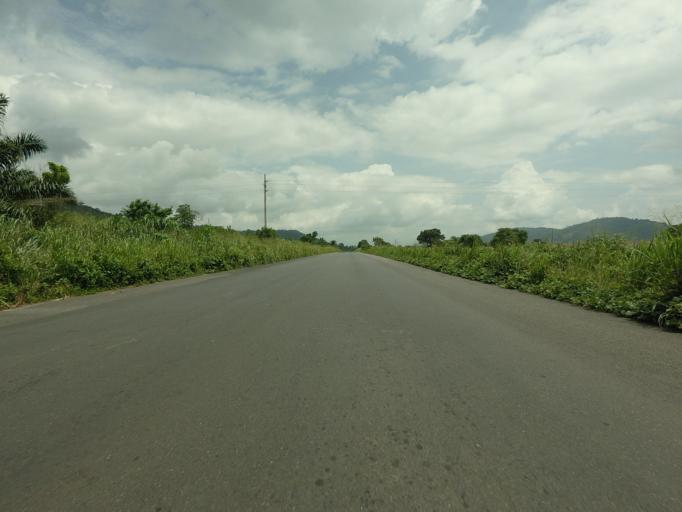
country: GH
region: Volta
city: Ho
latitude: 6.5545
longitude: 0.2587
